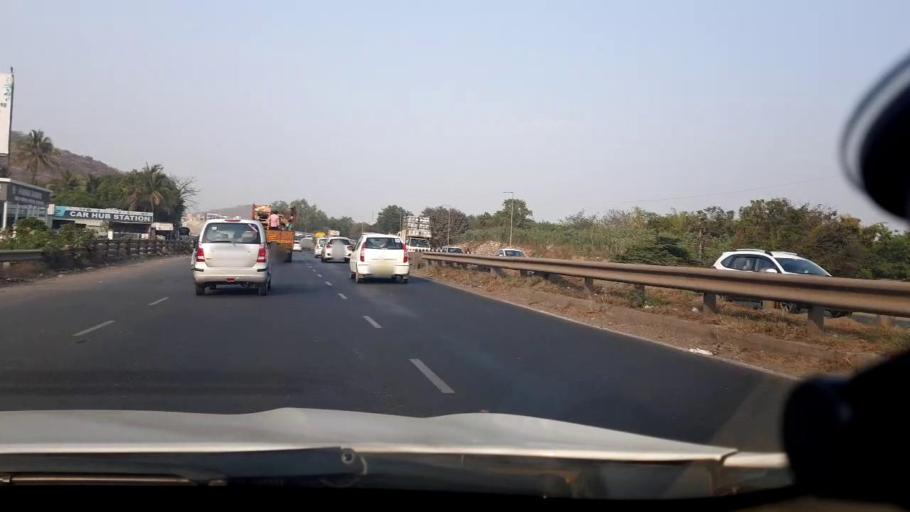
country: IN
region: Maharashtra
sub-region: Pune Division
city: Shivaji Nagar
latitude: 18.5310
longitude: 73.7792
